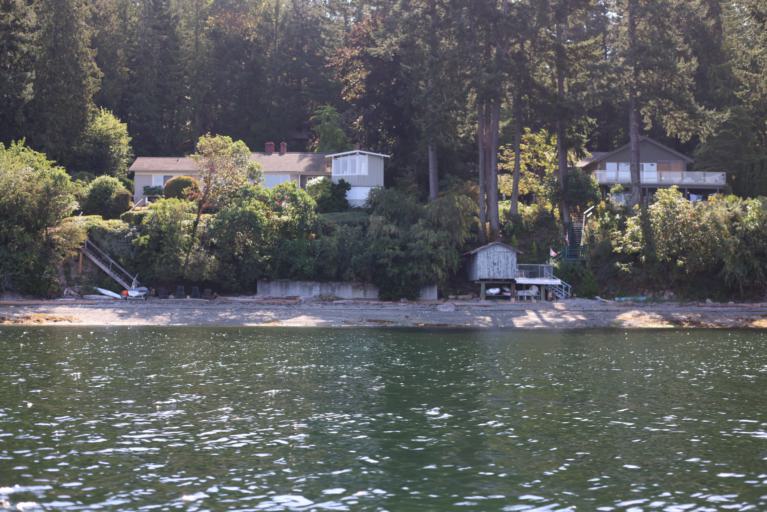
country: CA
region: British Columbia
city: North Saanich
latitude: 48.6403
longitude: -123.4754
